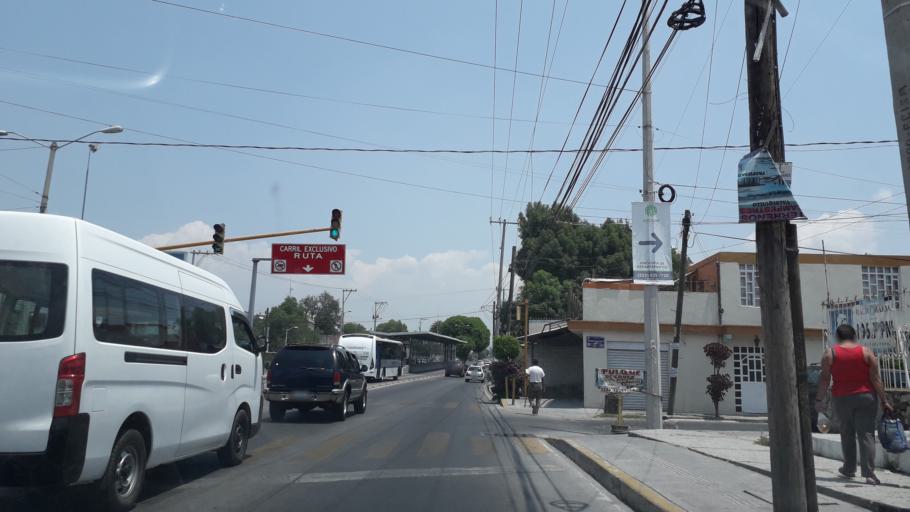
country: MX
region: Puebla
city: Puebla
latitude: 19.0213
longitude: -98.2263
